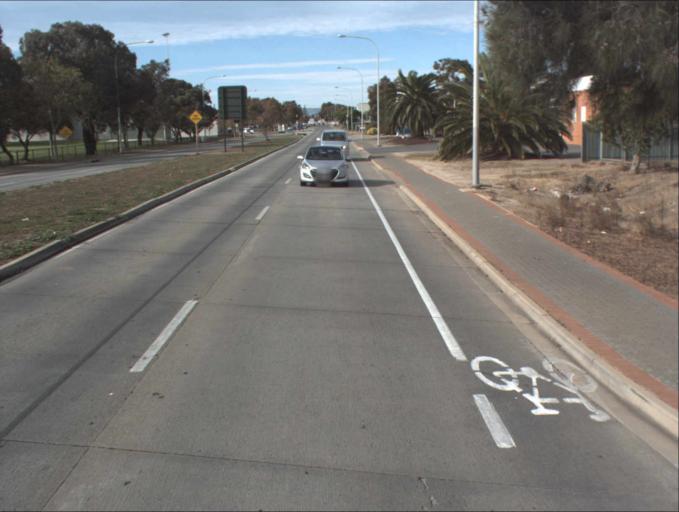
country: AU
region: South Australia
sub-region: Charles Sturt
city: West Lakes Shore
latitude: -34.8526
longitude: 138.5034
